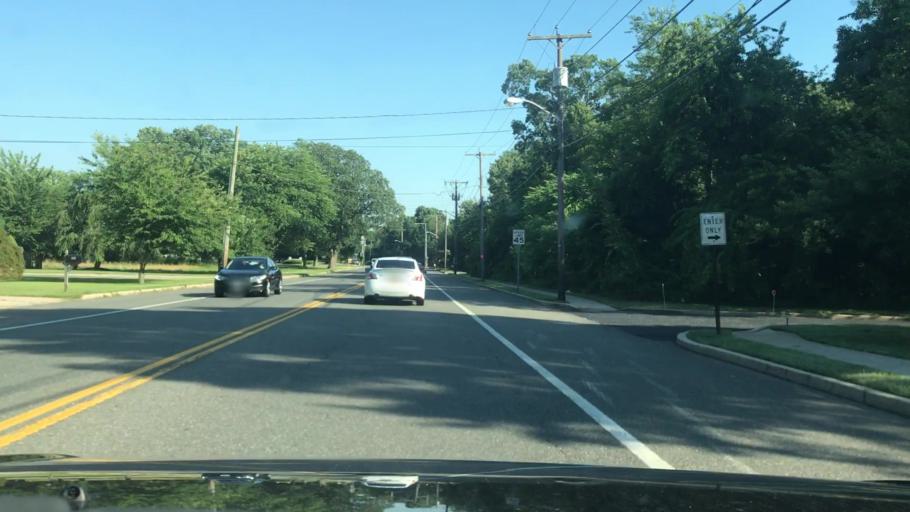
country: US
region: New Jersey
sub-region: Ocean County
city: Leisure Village
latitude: 40.0013
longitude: -74.2005
